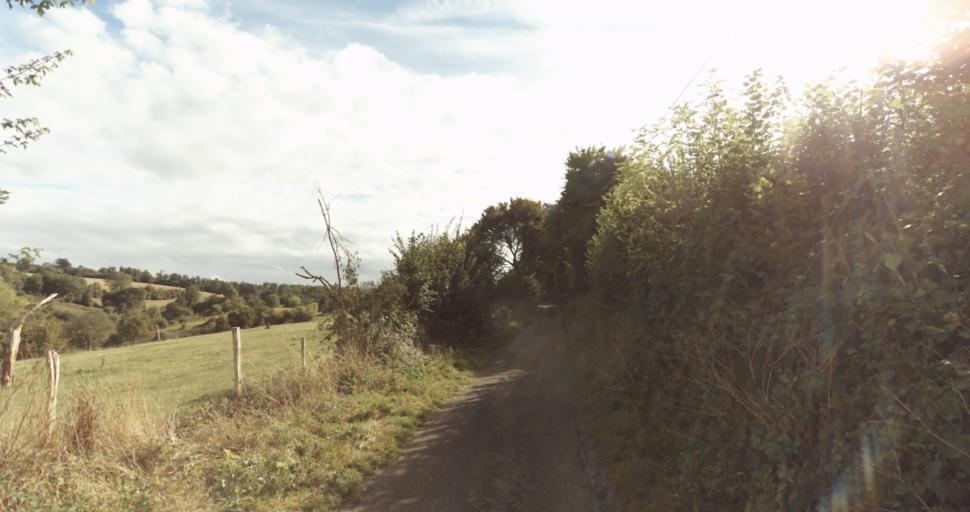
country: FR
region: Lower Normandy
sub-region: Departement de l'Orne
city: Vimoutiers
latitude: 48.8759
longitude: 0.1753
